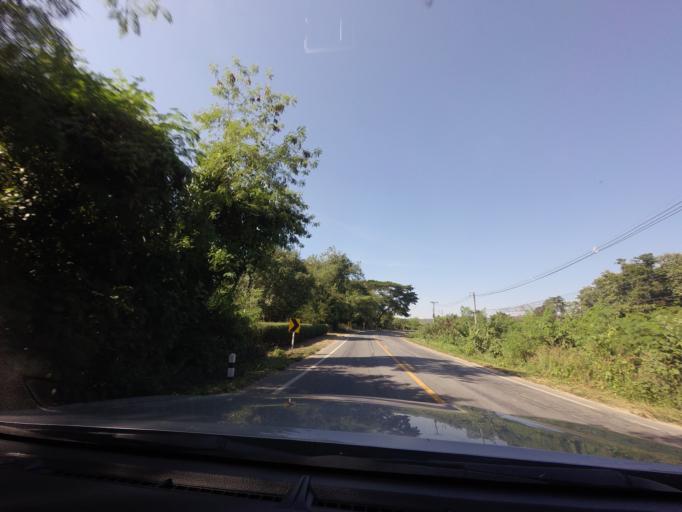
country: TH
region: Sukhothai
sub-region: Amphoe Si Satchanalai
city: Si Satchanalai
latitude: 17.6260
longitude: 99.7015
